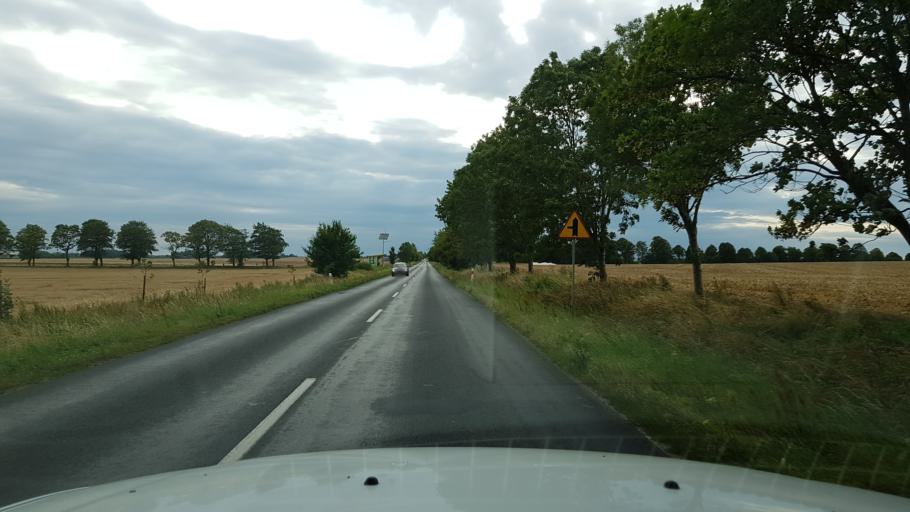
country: PL
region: West Pomeranian Voivodeship
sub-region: Powiat kolobrzeski
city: Dygowo
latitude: 54.1473
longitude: 15.6693
